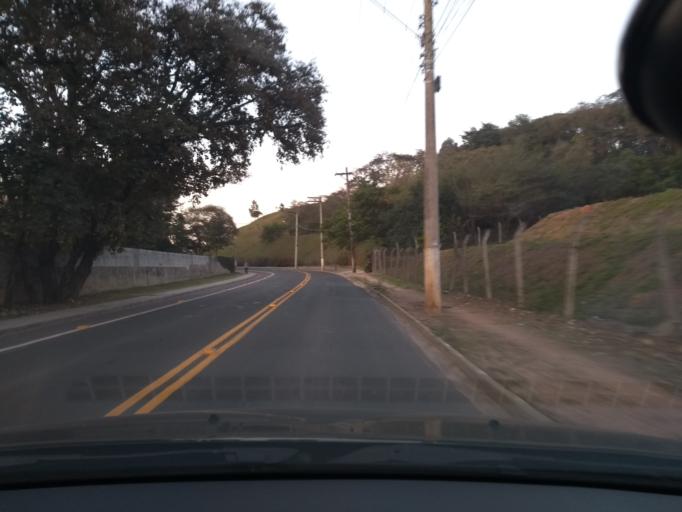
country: BR
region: Sao Paulo
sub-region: Itupeva
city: Itupeva
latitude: -23.1455
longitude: -47.0433
